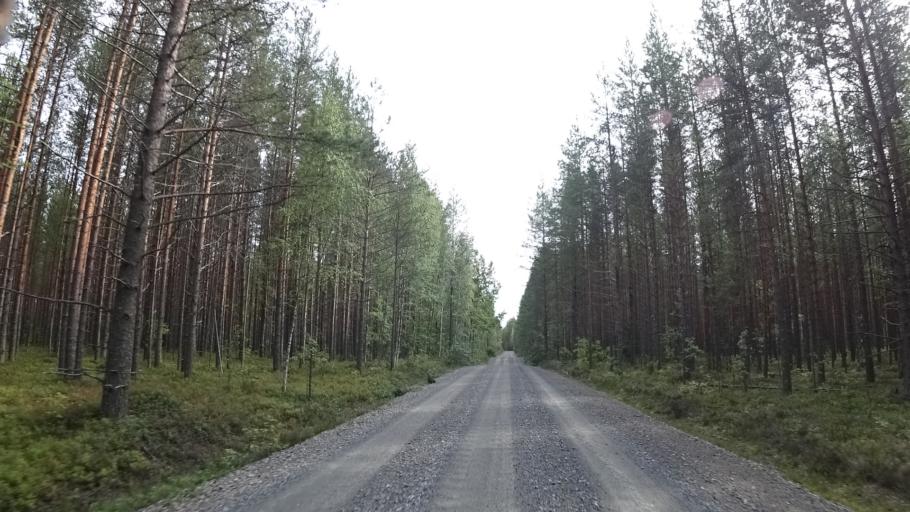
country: FI
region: North Karelia
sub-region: Joensuu
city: Ilomantsi
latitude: 62.6072
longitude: 31.1855
